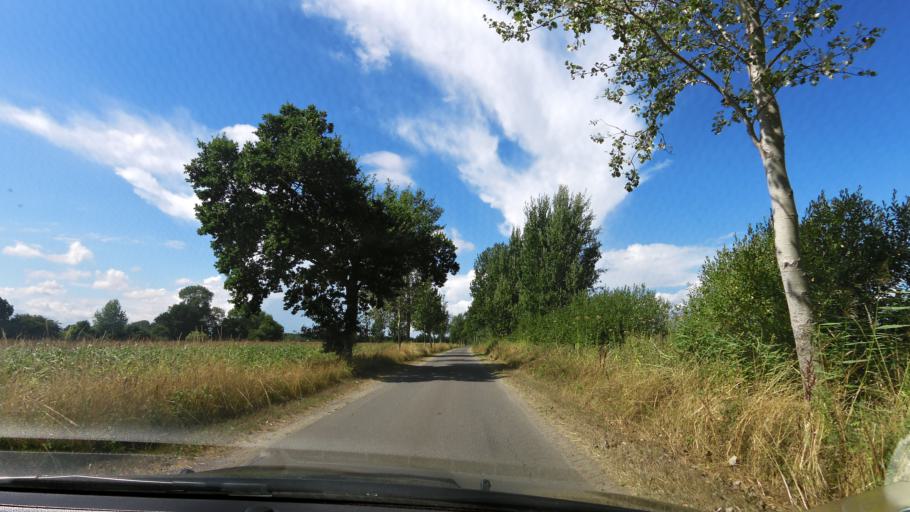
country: DK
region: South Denmark
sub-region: Nordfyns Kommune
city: Otterup
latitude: 55.5435
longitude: 10.4694
